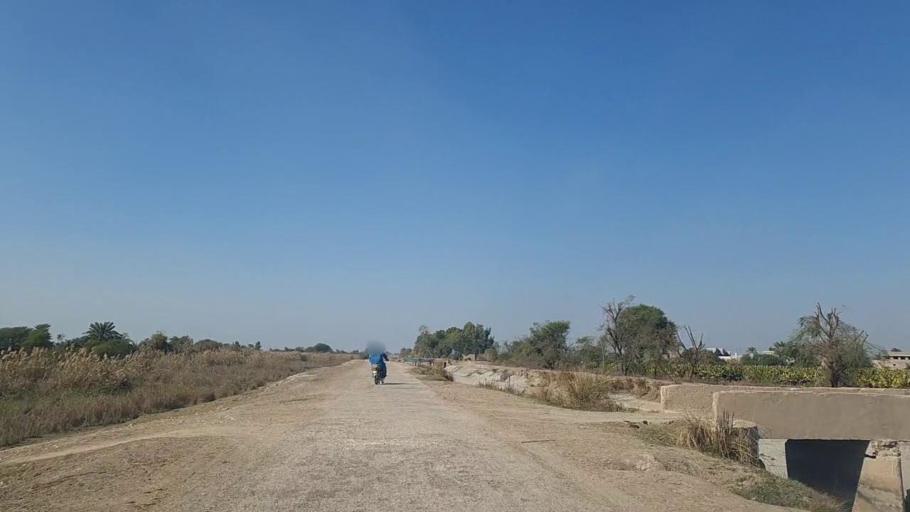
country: PK
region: Sindh
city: Jam Sahib
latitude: 26.2211
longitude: 68.6027
